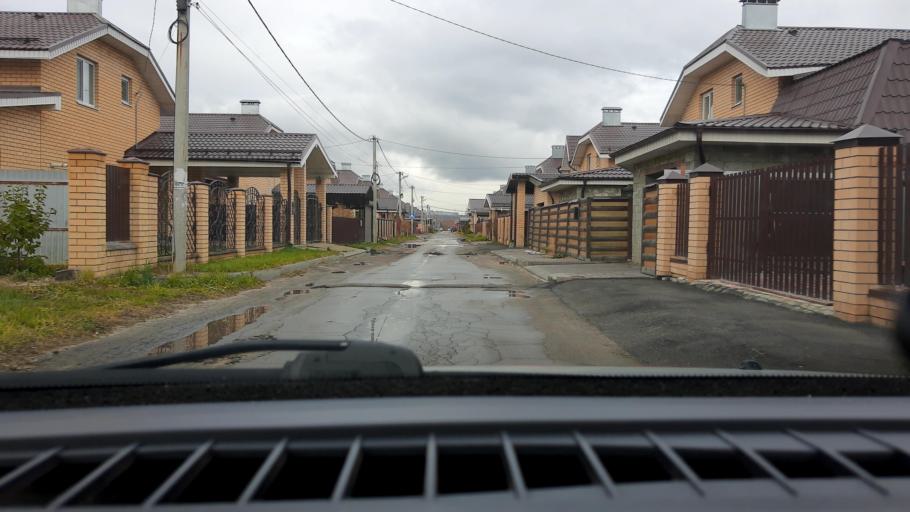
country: RU
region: Nizjnij Novgorod
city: Afonino
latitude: 56.2015
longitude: 44.1289
